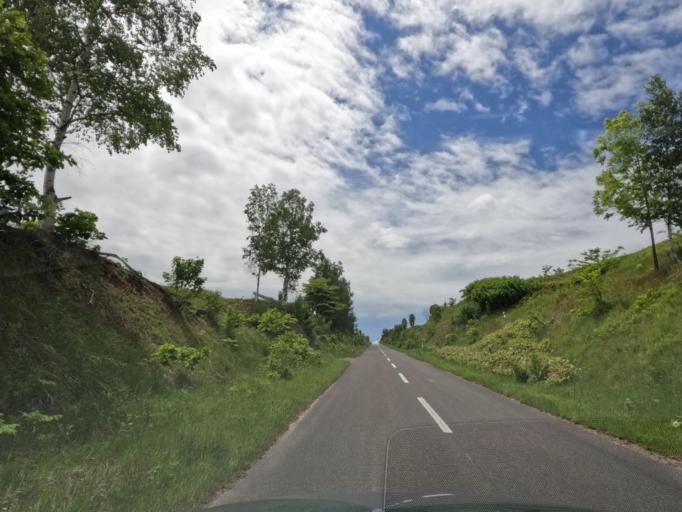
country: JP
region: Hokkaido
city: Shimo-furano
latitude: 43.5127
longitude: 142.4236
